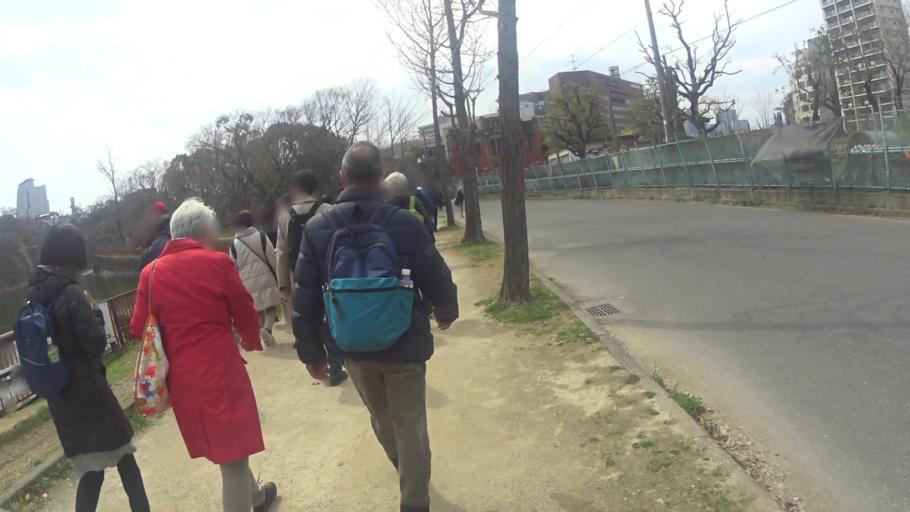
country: JP
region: Osaka
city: Osaka-shi
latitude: 34.6905
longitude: 135.5237
